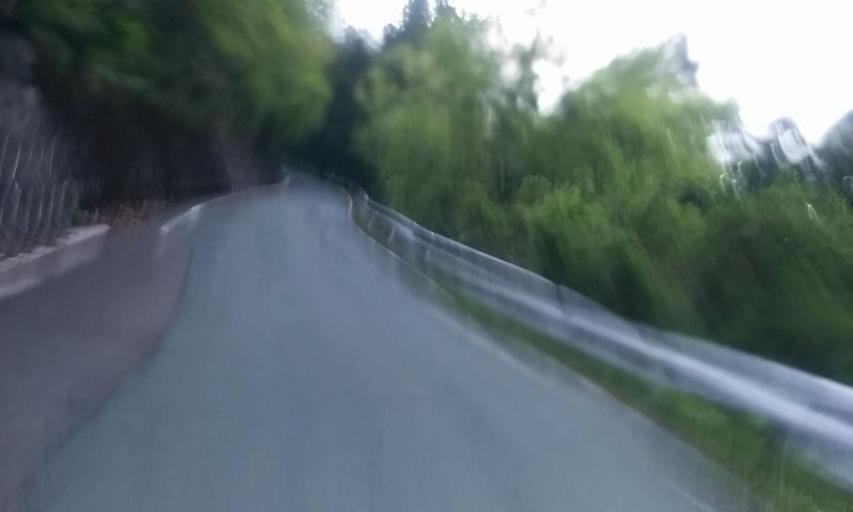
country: JP
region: Ehime
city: Saijo
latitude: 33.8017
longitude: 133.2755
